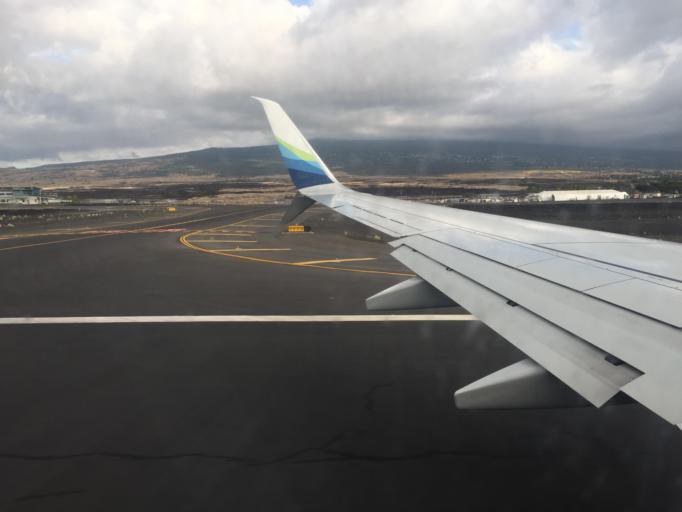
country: US
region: Hawaii
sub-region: Hawaii County
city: Kalaoa
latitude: 19.7412
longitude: -156.0454
